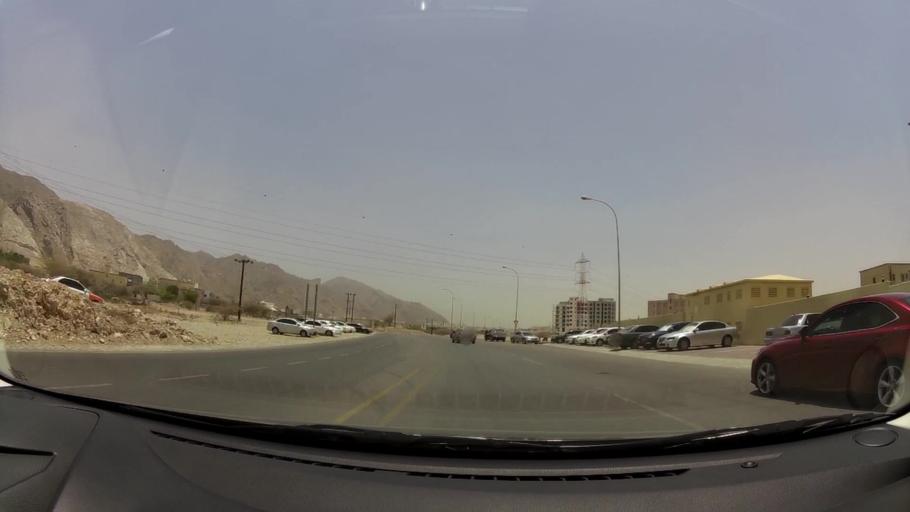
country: OM
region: Muhafazat Masqat
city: Bawshar
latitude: 23.5564
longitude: 58.4106
